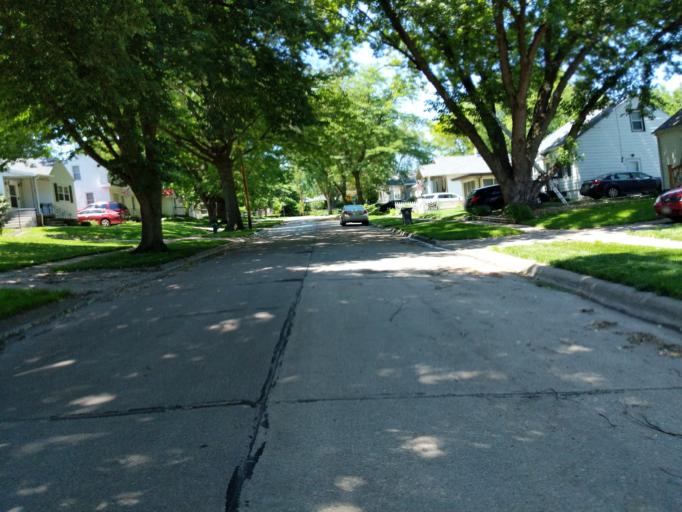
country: US
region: Iowa
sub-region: Linn County
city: Cedar Rapids
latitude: 42.0187
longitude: -91.6348
